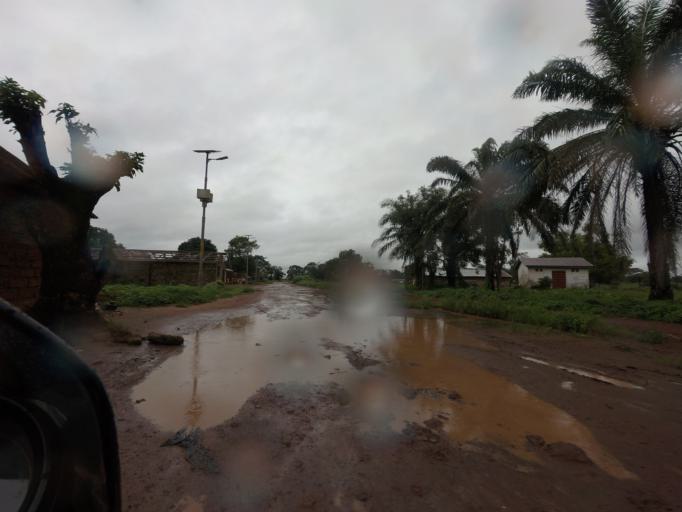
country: SL
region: Northern Province
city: Kambia
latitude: 9.1120
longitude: -12.9244
